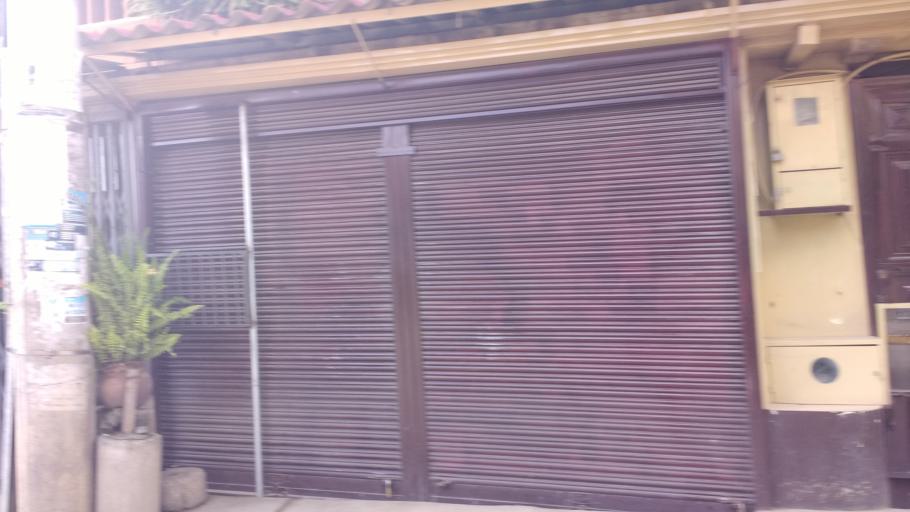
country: EC
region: Azuay
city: Cuenca
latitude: -2.8961
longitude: -79.0519
